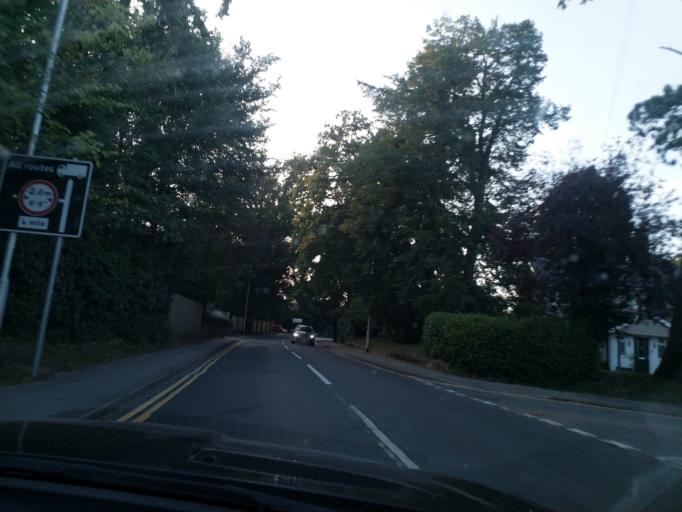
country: GB
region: England
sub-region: Wokingham
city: Wokingham
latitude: 51.4067
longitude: -0.8236
